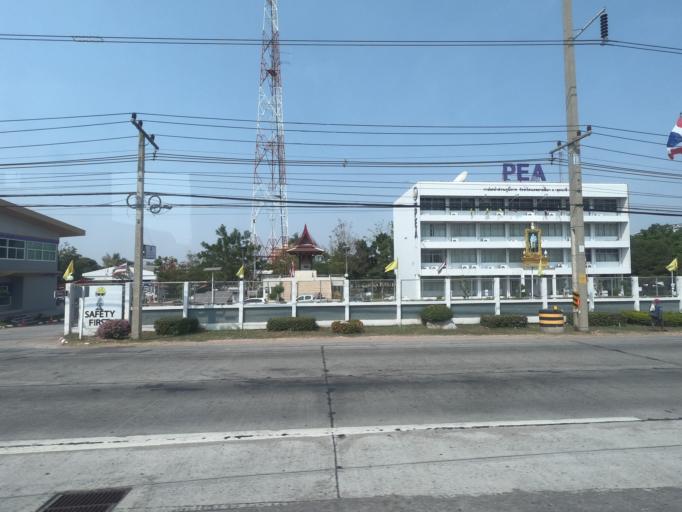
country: TH
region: Nakhon Ratchasima
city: Kham Thale So
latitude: 14.9481
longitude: 102.0157
